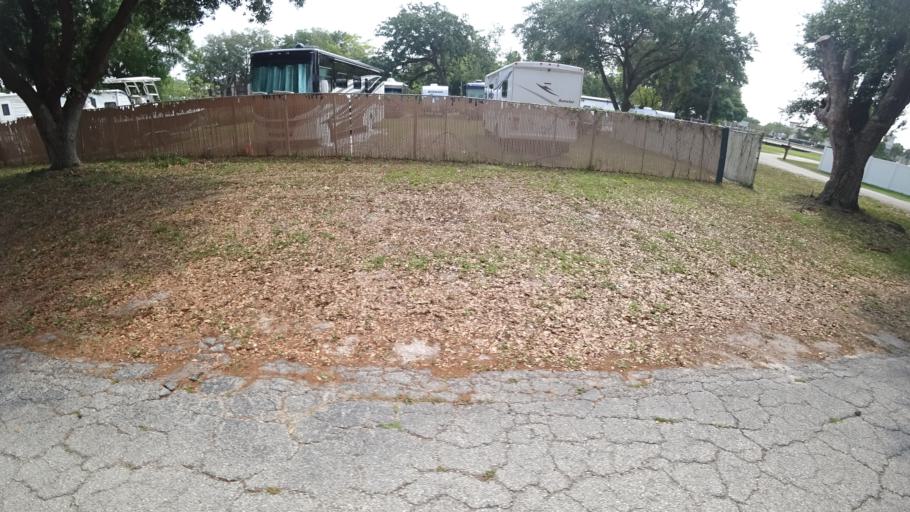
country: US
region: Florida
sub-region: Manatee County
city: Samoset
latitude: 27.4470
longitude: -82.5074
